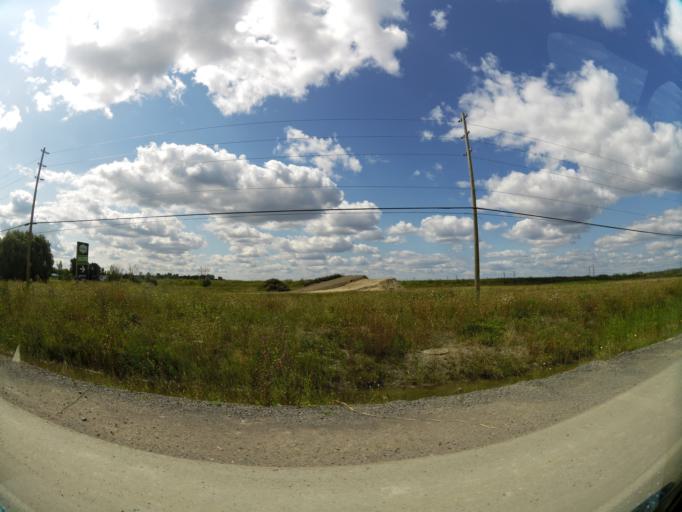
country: CA
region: Ontario
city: Ottawa
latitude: 45.4402
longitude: -75.4954
